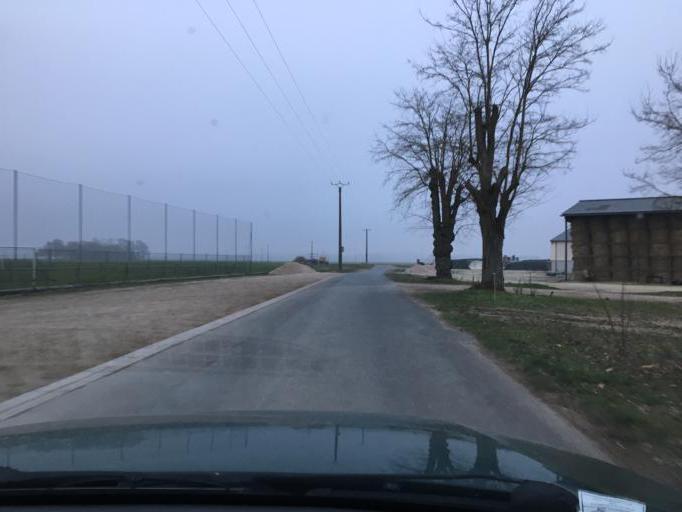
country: FR
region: Centre
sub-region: Departement du Loiret
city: Beaugency
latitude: 47.7710
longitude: 1.6440
